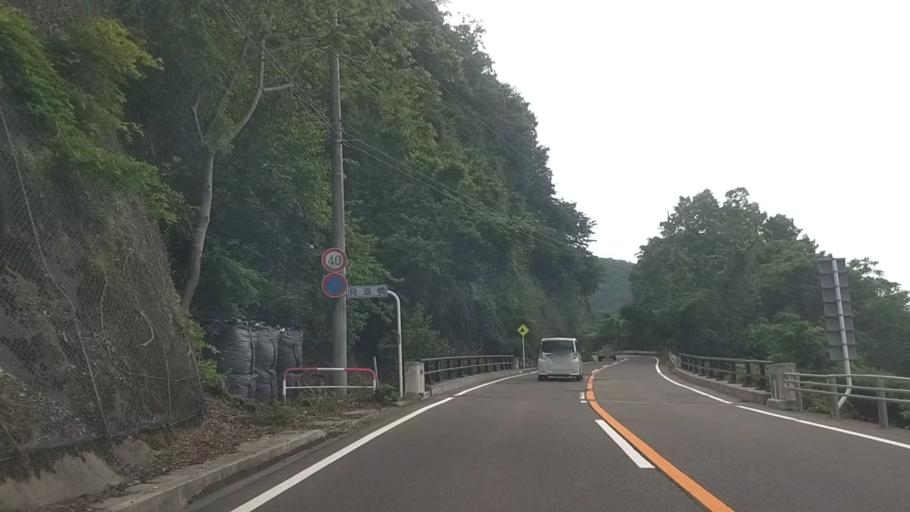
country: JP
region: Yamanashi
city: Fujikawaguchiko
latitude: 35.5210
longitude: 138.6217
